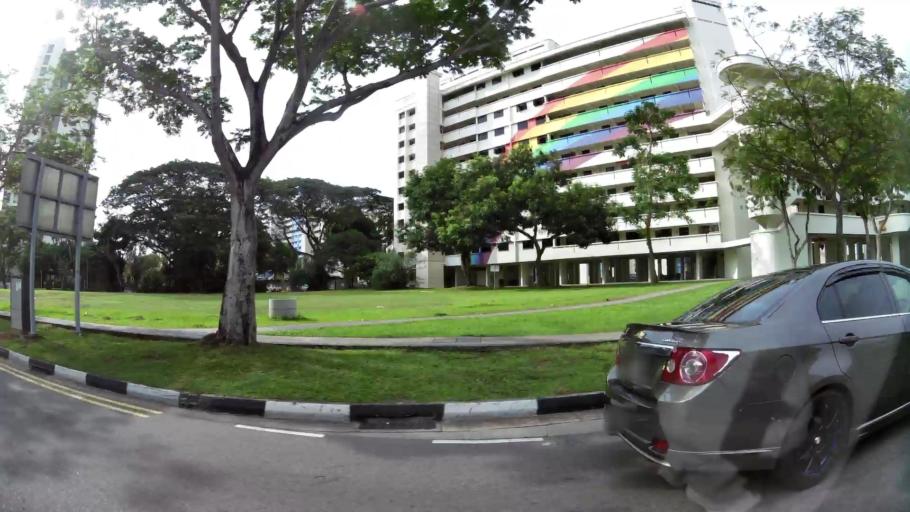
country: SG
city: Singapore
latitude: 1.3645
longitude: 103.8967
